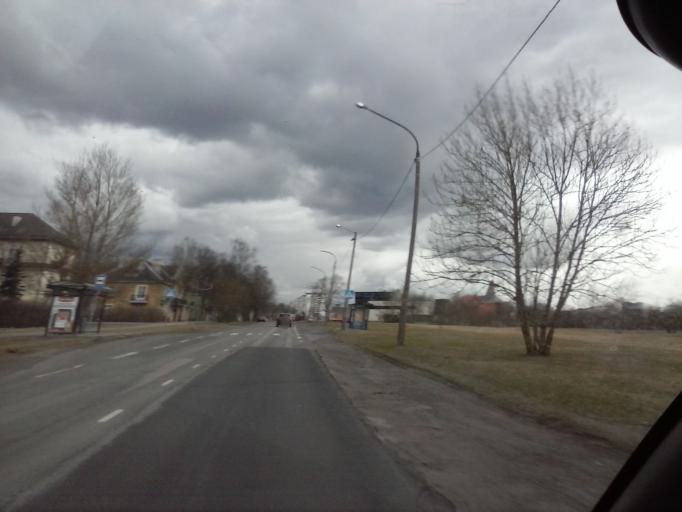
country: EE
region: Harju
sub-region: Tallinna linn
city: Tallinn
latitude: 59.4382
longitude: 24.8028
